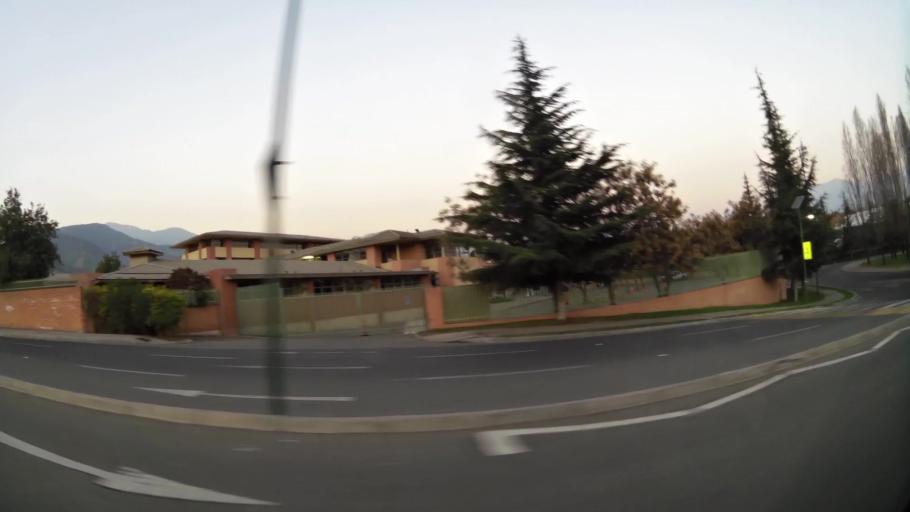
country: CL
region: Santiago Metropolitan
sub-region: Provincia de Chacabuco
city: Chicureo Abajo
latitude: -33.3249
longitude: -70.5424
